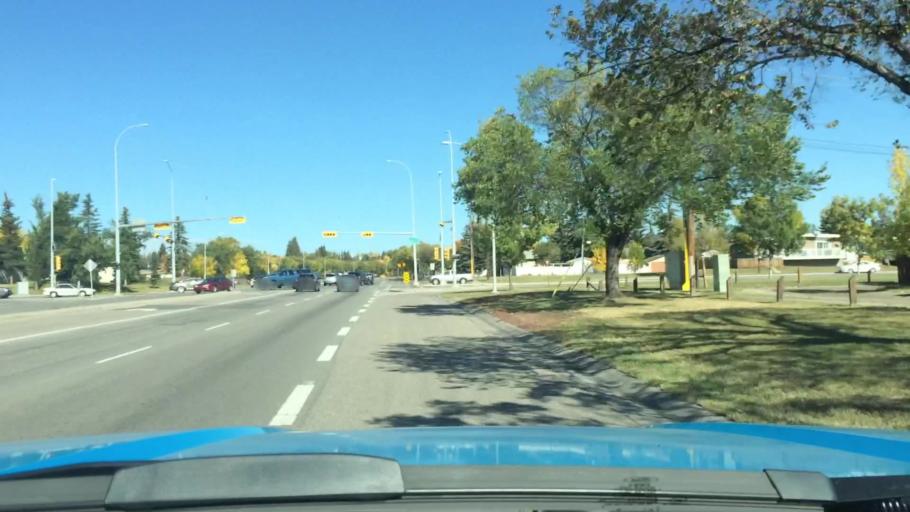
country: CA
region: Alberta
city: Calgary
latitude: 51.1173
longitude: -114.0689
